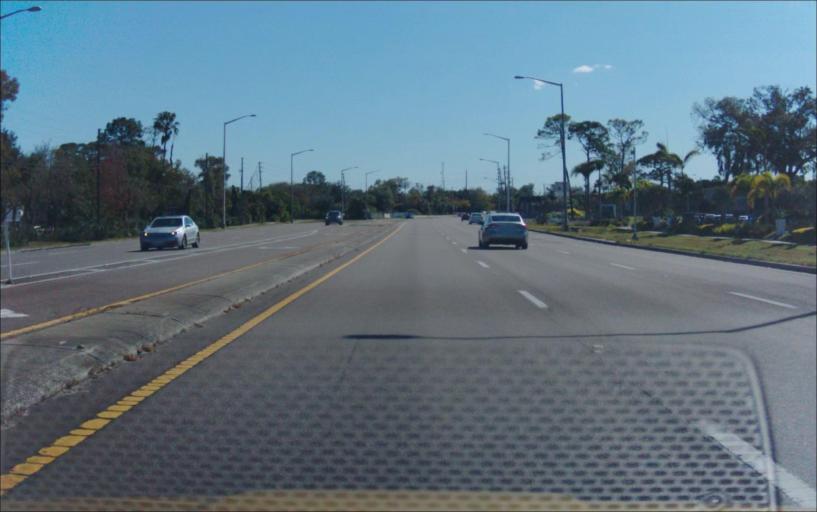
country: US
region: Florida
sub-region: Seminole County
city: Goldenrod
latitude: 28.5996
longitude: -81.2999
